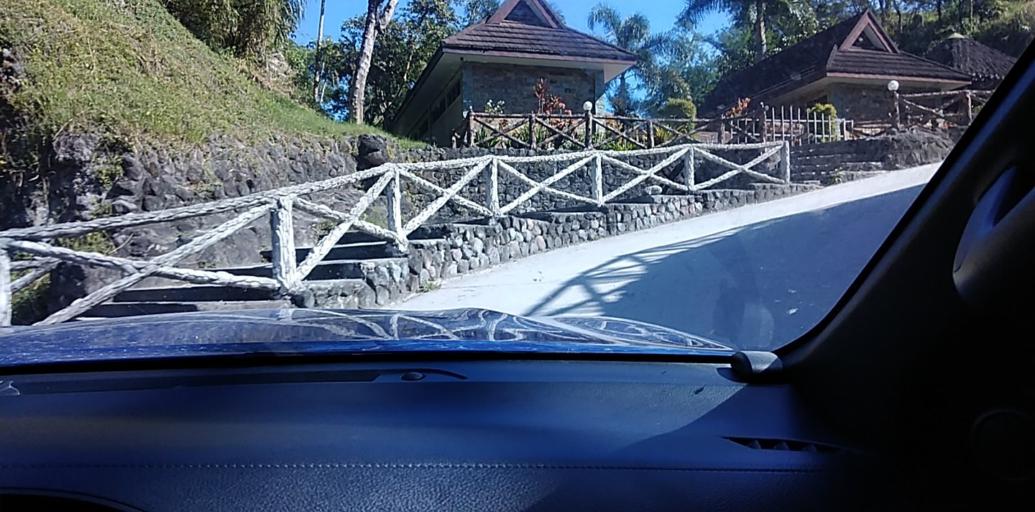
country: PH
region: Central Luzon
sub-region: Province of Pampanga
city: Dolores
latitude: 15.1702
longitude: 120.4724
